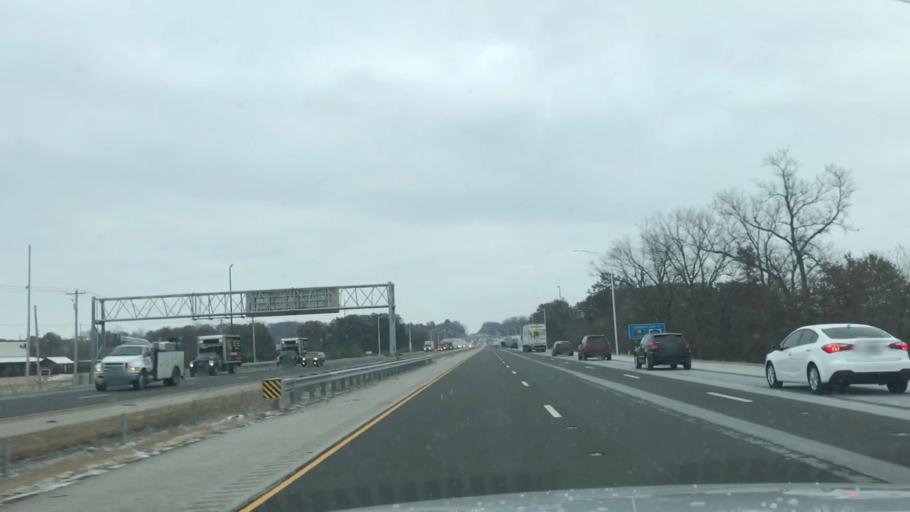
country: US
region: Illinois
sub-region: Madison County
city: Glen Carbon
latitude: 38.7567
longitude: -90.0234
